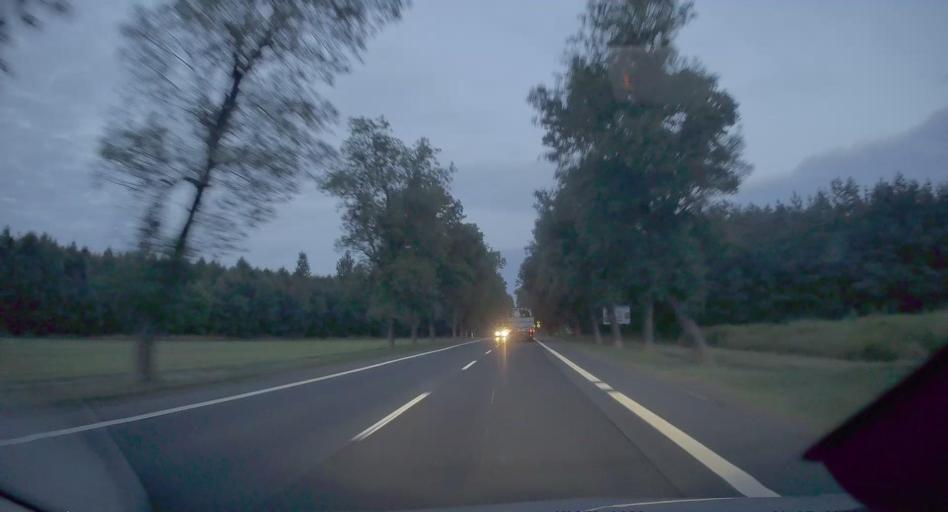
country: PL
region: Silesian Voivodeship
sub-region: Powiat klobucki
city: Klobuck
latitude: 50.9216
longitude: 18.8791
